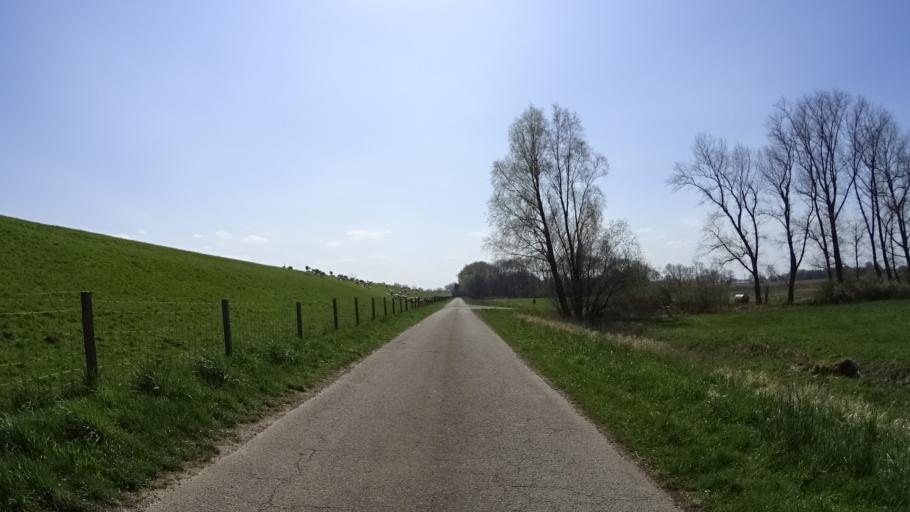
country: DE
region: Lower Saxony
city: Weener
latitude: 53.1208
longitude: 7.3721
